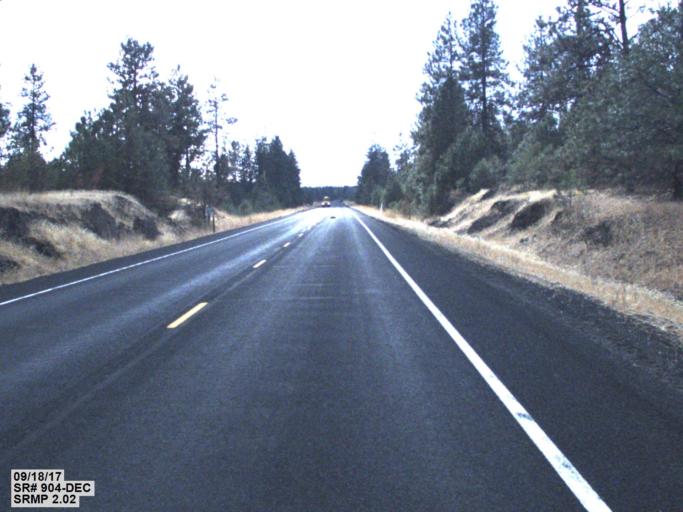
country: US
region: Washington
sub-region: Spokane County
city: Medical Lake
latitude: 47.4435
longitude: -117.7507
